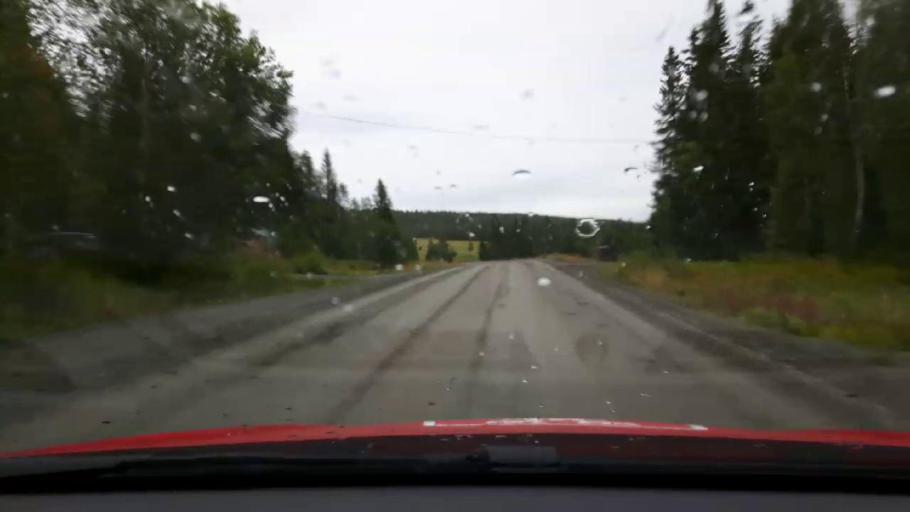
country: SE
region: Jaemtland
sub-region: Are Kommun
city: Are
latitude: 63.4635
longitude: 12.6248
